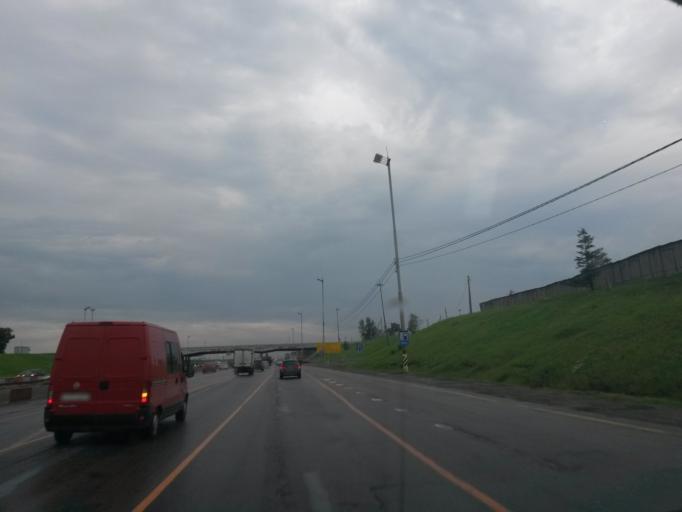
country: RU
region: Moskovskaya
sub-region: Podol'skiy Rayon
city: Podol'sk
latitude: 55.4395
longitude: 37.6156
